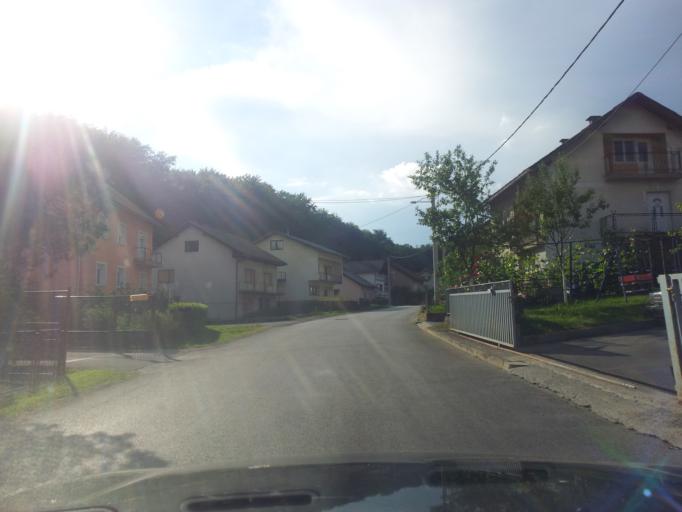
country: HR
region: Karlovacka
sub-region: Grad Karlovac
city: Karlovac
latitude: 45.4600
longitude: 15.4820
